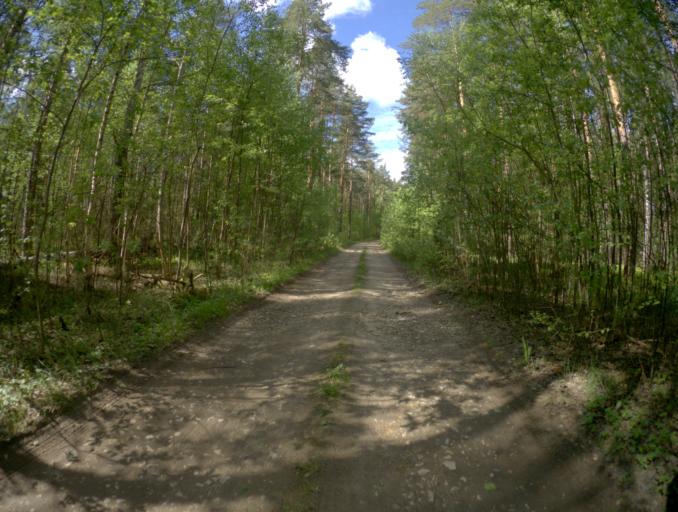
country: RU
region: Rjazan
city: Spas-Klepiki
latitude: 55.2430
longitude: 40.0688
